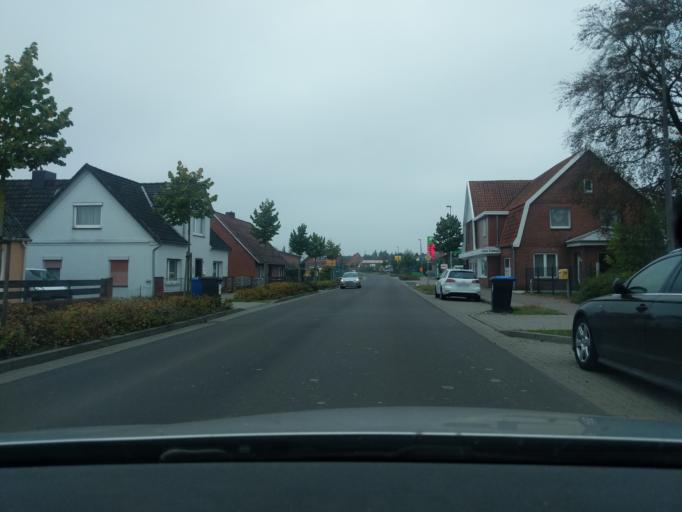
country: DE
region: Lower Saxony
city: Hemmoor
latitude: 53.6803
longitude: 9.1798
